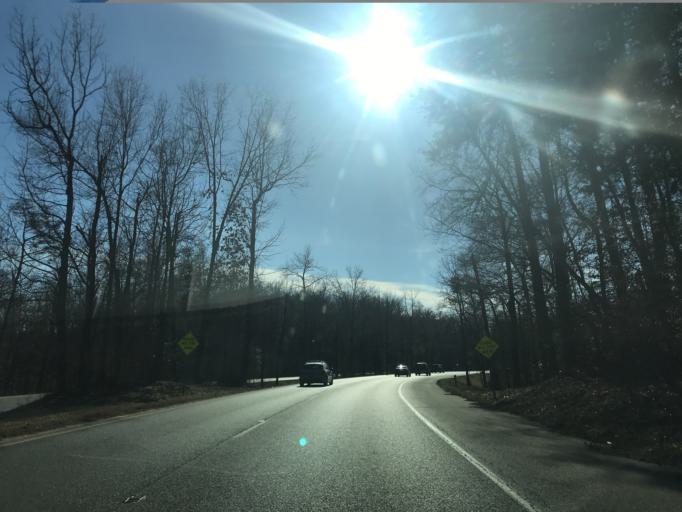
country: US
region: Maryland
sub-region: Charles County
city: Saint Charles
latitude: 38.6124
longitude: -76.8837
